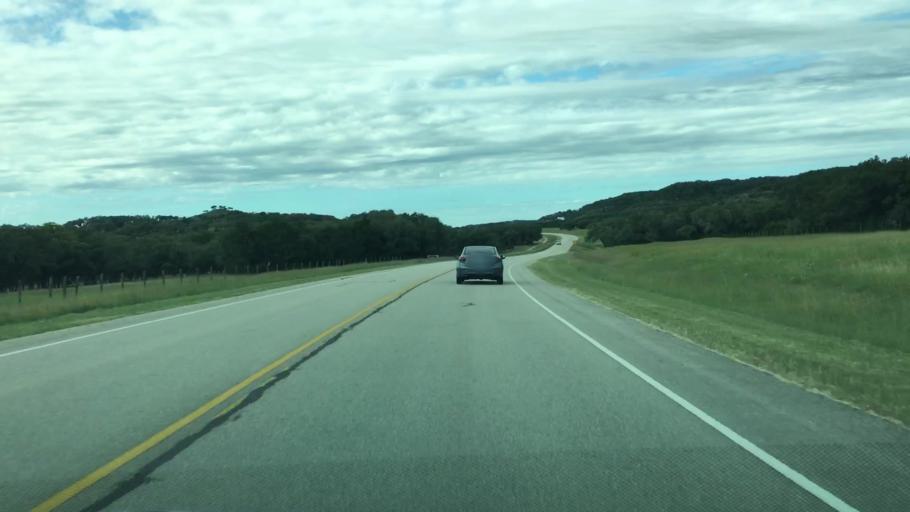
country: US
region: Texas
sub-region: Hays County
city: Wimberley
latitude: 30.0106
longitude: -98.0840
